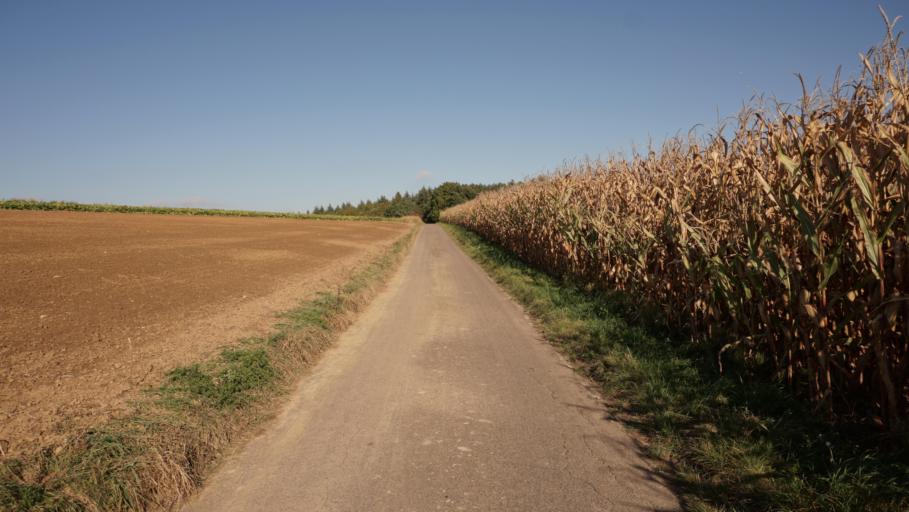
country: DE
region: Baden-Wuerttemberg
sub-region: Karlsruhe Region
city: Billigheim
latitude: 49.3581
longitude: 9.2362
